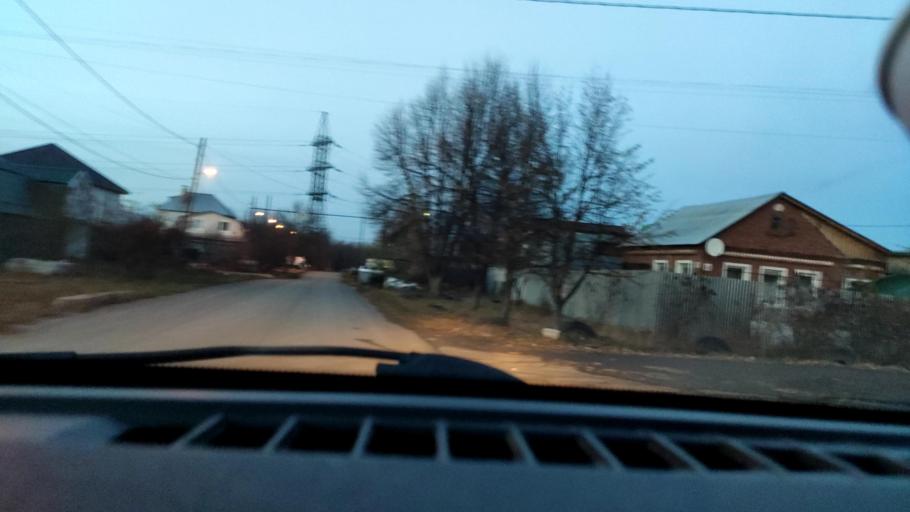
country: RU
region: Samara
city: Petra-Dubrava
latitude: 53.2629
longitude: 50.3301
